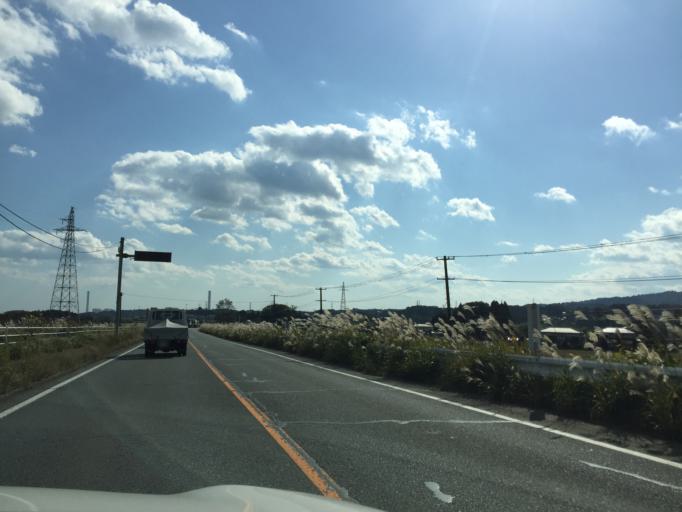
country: JP
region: Fukushima
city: Namie
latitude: 37.2798
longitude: 140.9933
